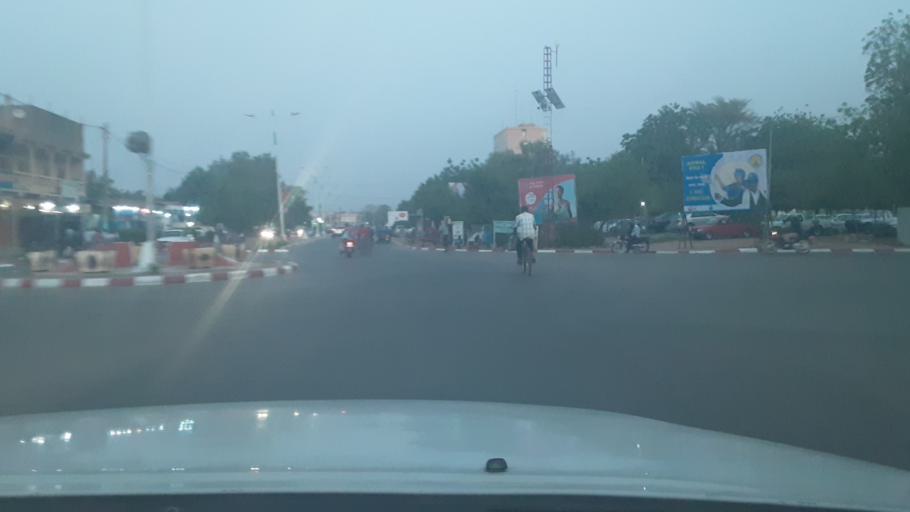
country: TD
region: Chari-Baguirmi
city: N'Djamena
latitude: 12.0951
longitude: 15.0693
